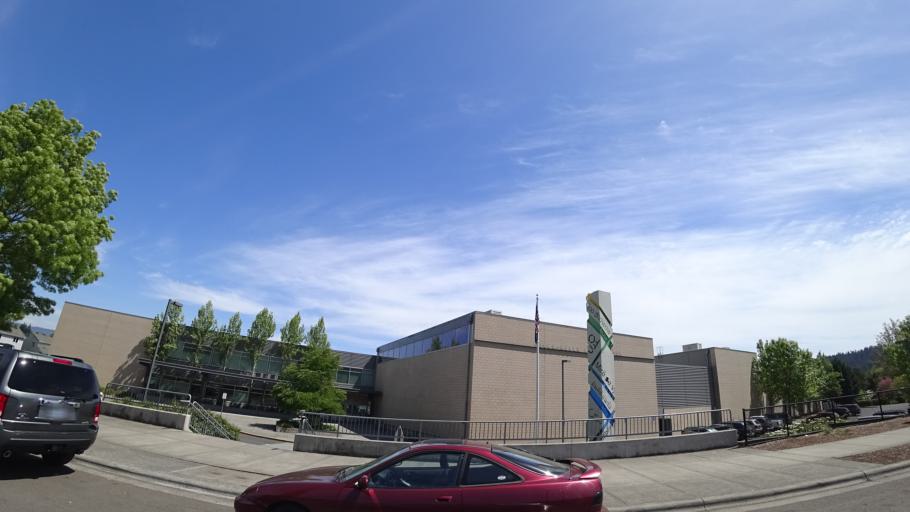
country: US
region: Oregon
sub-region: Washington County
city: Aloha
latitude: 45.4837
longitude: -122.8547
